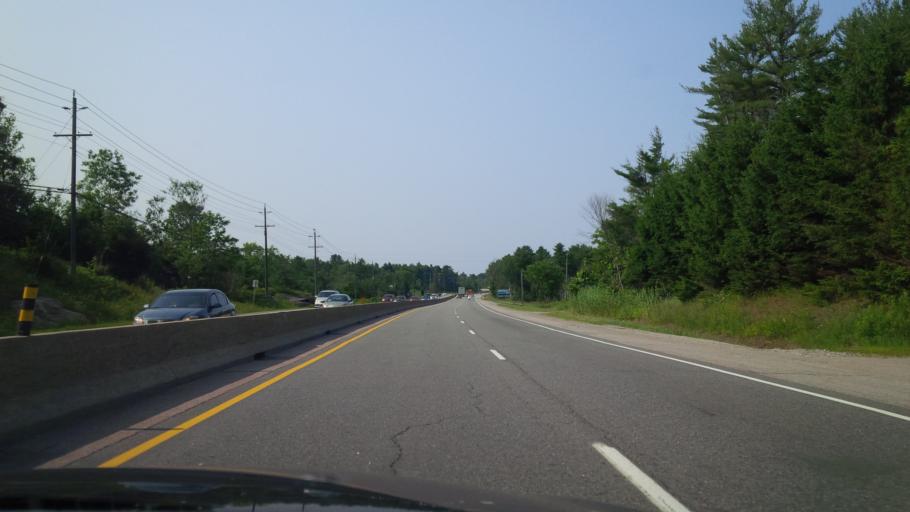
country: CA
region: Ontario
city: Gravenhurst
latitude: 44.8060
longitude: -79.3278
